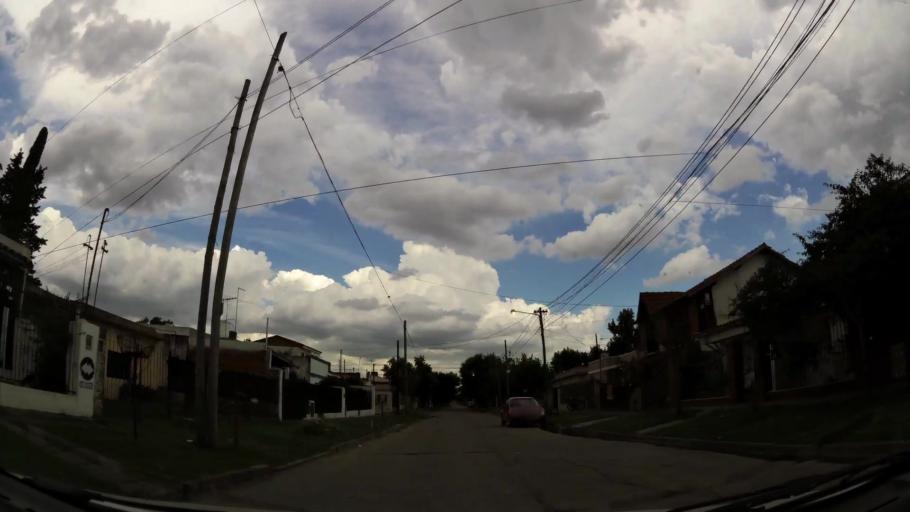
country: AR
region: Buenos Aires
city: Ituzaingo
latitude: -34.6389
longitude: -58.6867
